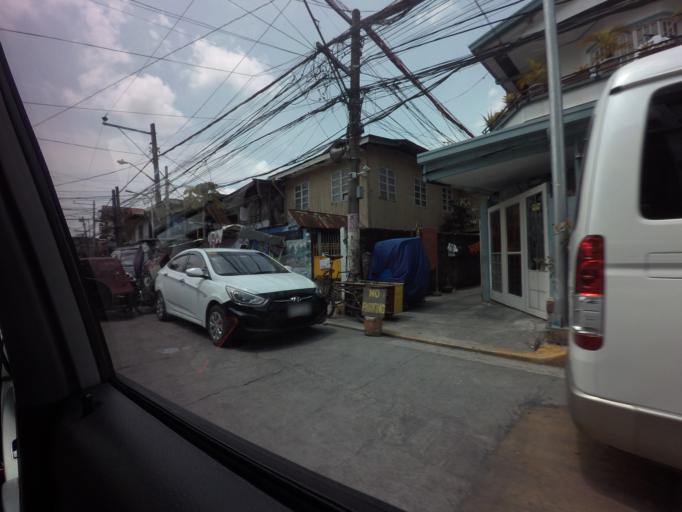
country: PH
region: Metro Manila
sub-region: City of Manila
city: Quiapo
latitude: 14.5853
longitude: 121.0035
